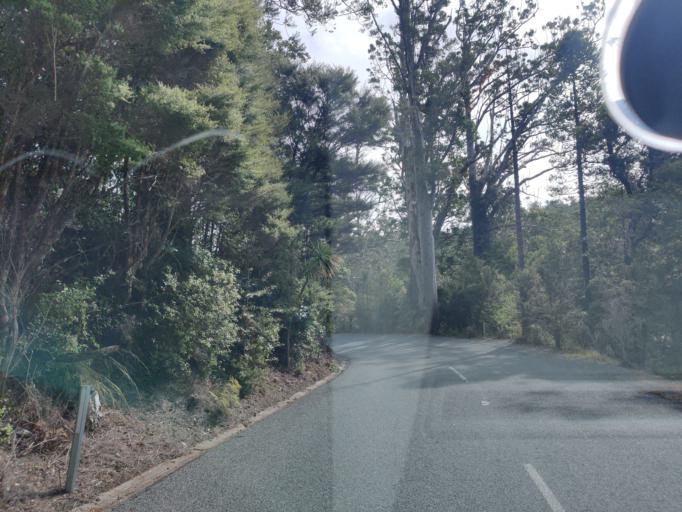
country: NZ
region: Northland
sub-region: Kaipara District
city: Dargaville
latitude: -35.6460
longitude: 173.5579
